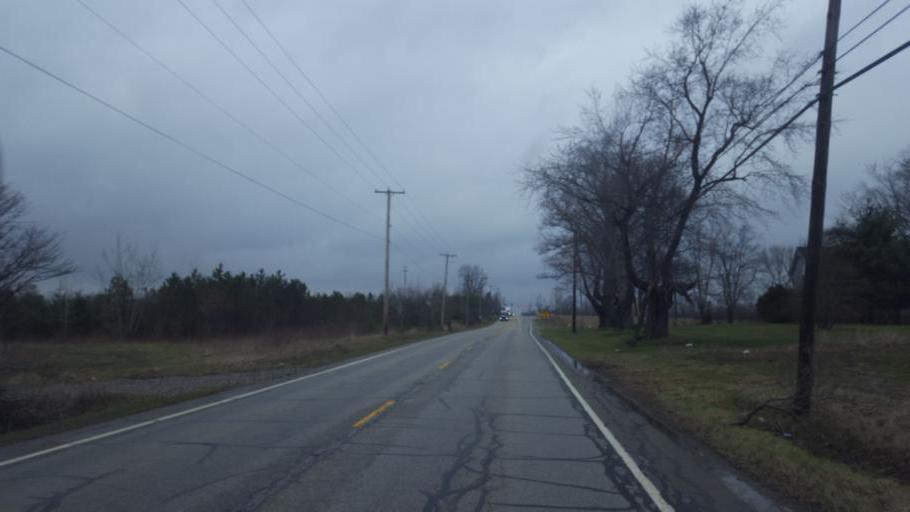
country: US
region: Ohio
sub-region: Medina County
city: Medina
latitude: 41.0960
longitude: -81.8642
